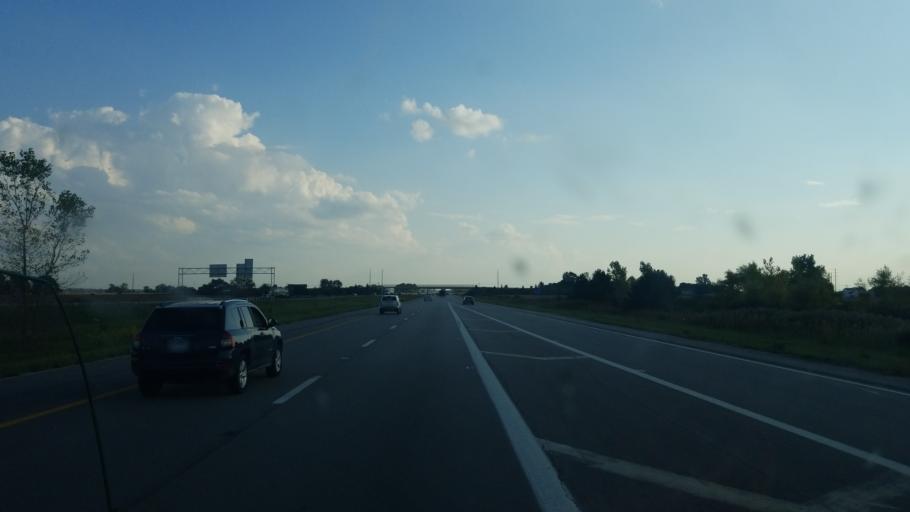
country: US
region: Ohio
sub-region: Wood County
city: Perrysburg
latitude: 41.5277
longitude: -83.6221
